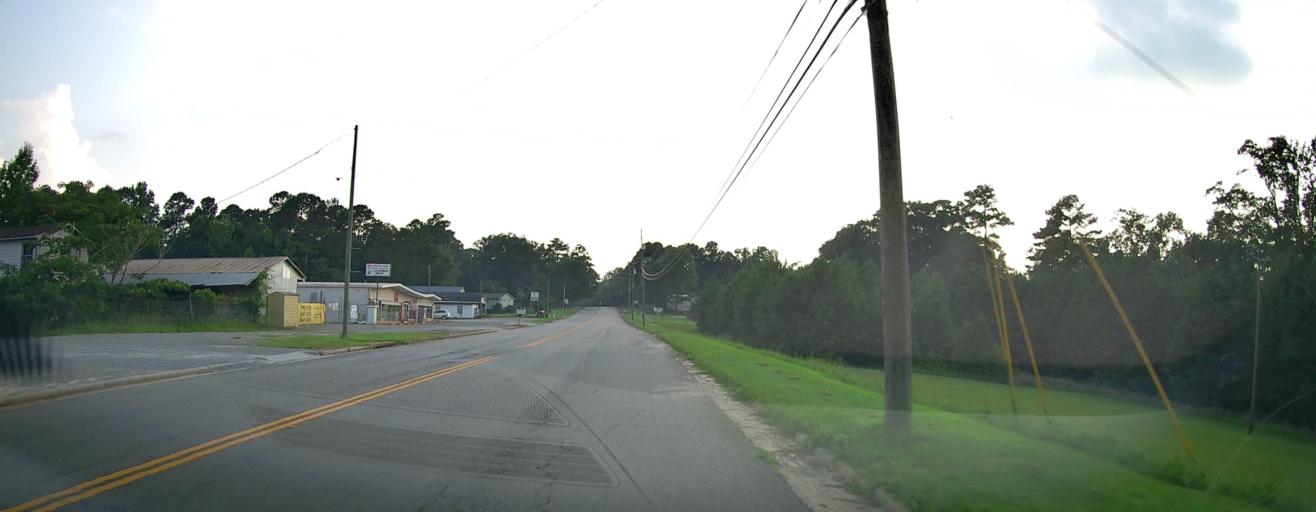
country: US
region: Georgia
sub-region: Jones County
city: Gray
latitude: 33.0138
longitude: -83.5242
